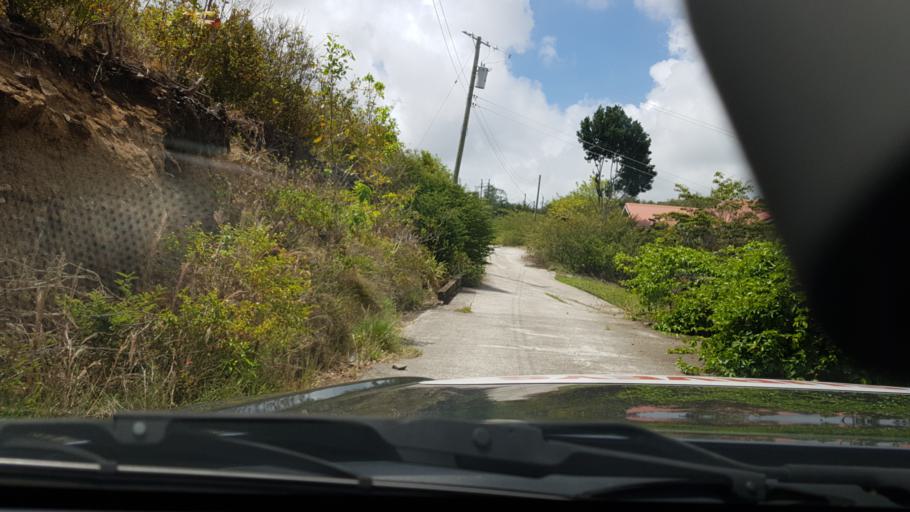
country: LC
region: Gros-Islet
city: Gros Islet
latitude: 14.0646
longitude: -60.9295
